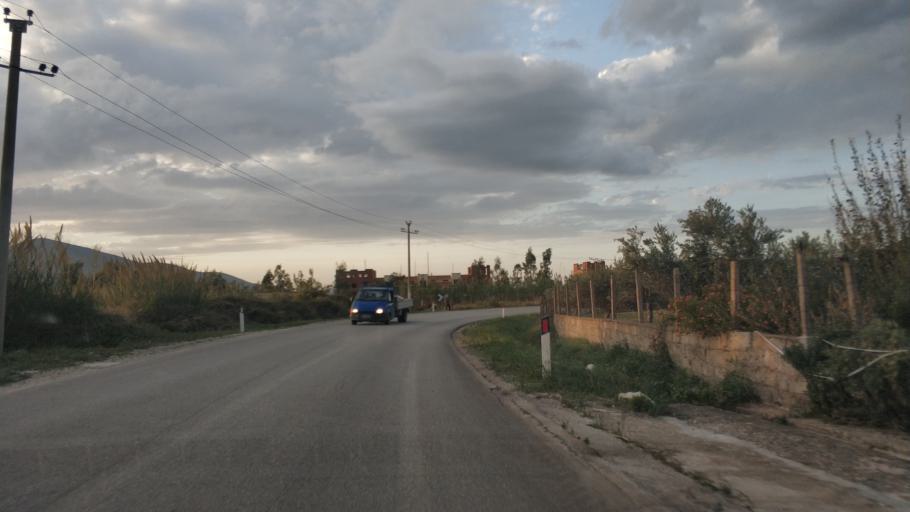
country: AL
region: Vlore
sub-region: Rrethi i Vlores
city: Orikum
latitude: 40.3368
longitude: 19.4757
